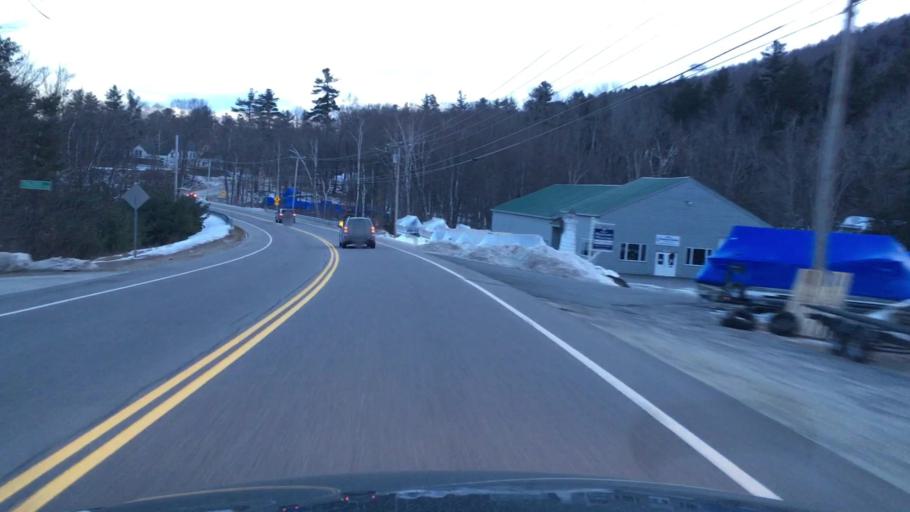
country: US
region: New Hampshire
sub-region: Merrimack County
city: Newbury
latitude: 43.3240
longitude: -72.0421
